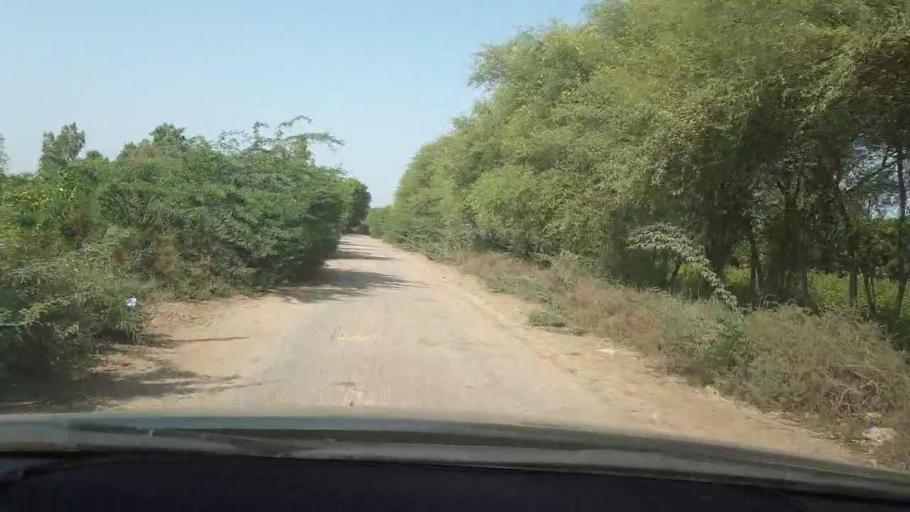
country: PK
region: Sindh
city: Naukot
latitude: 24.7665
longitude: 69.2285
